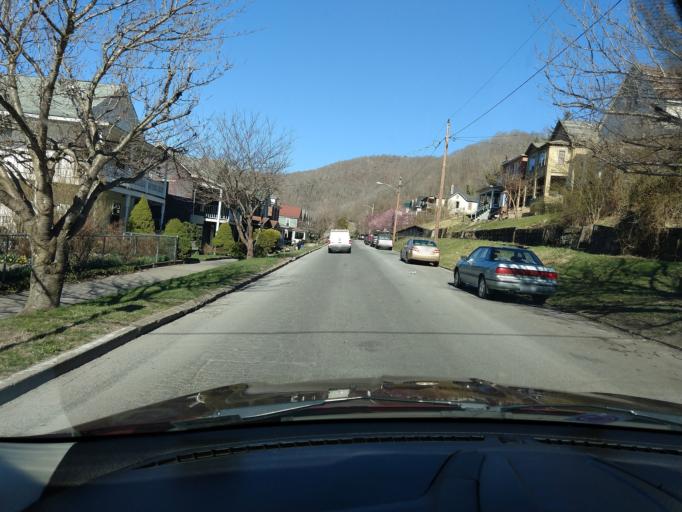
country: US
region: West Virginia
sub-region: Summers County
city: Hinton
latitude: 37.6777
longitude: -80.8806
